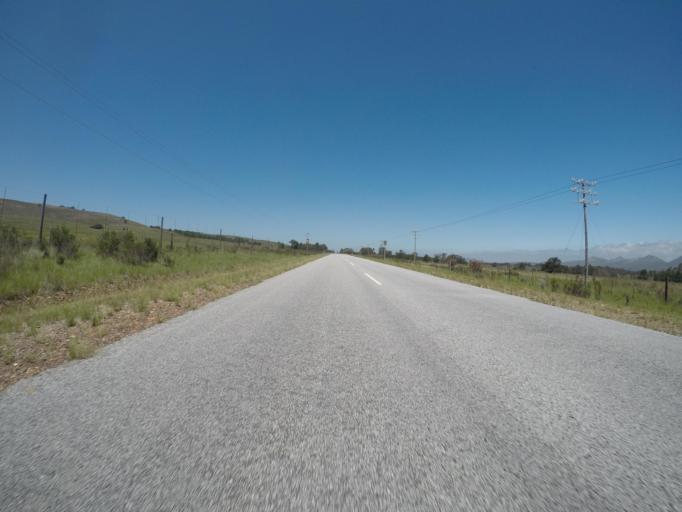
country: ZA
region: Eastern Cape
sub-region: Cacadu District Municipality
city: Kareedouw
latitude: -33.9671
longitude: 24.4489
